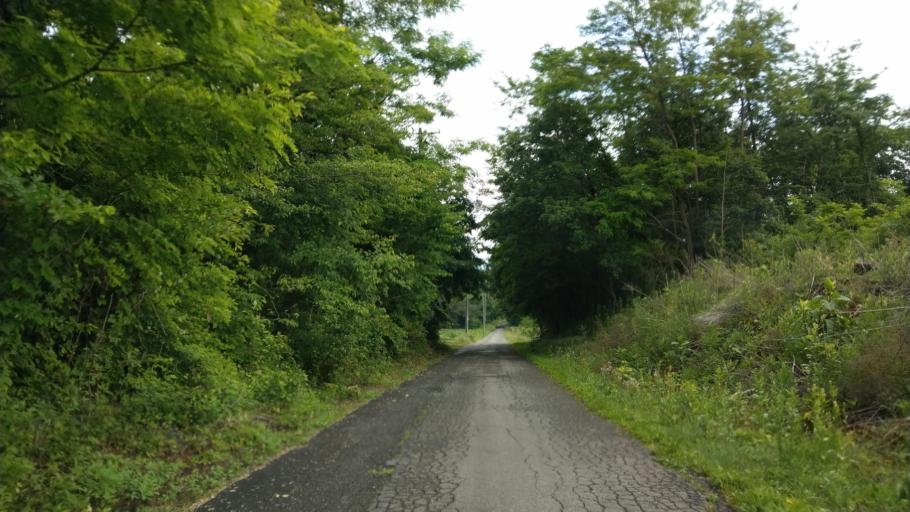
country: JP
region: Nagano
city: Komoro
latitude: 36.2873
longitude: 138.3756
